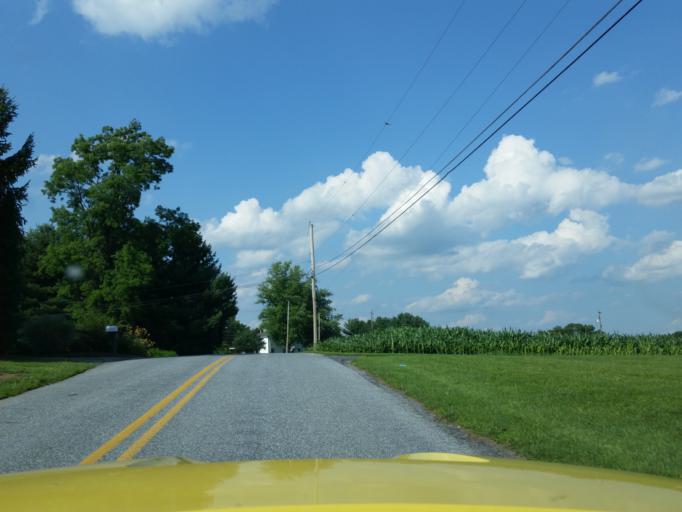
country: US
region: Pennsylvania
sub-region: Lebanon County
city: Annville
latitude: 40.3798
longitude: -76.5299
